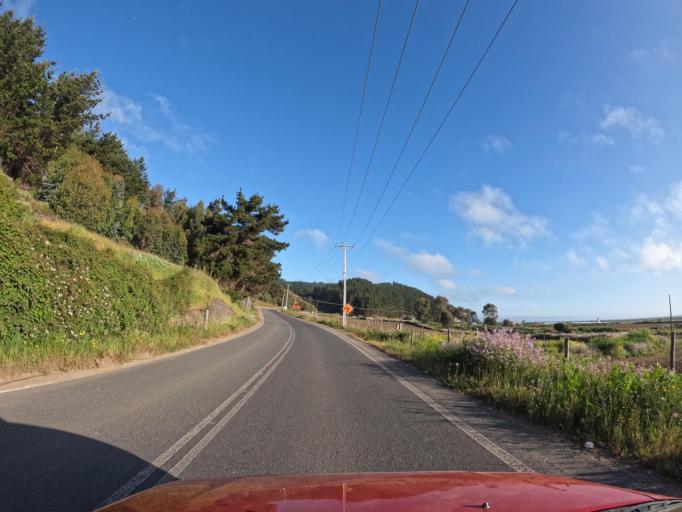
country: CL
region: Maule
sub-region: Provincia de Talca
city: Constitucion
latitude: -34.9837
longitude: -72.1797
